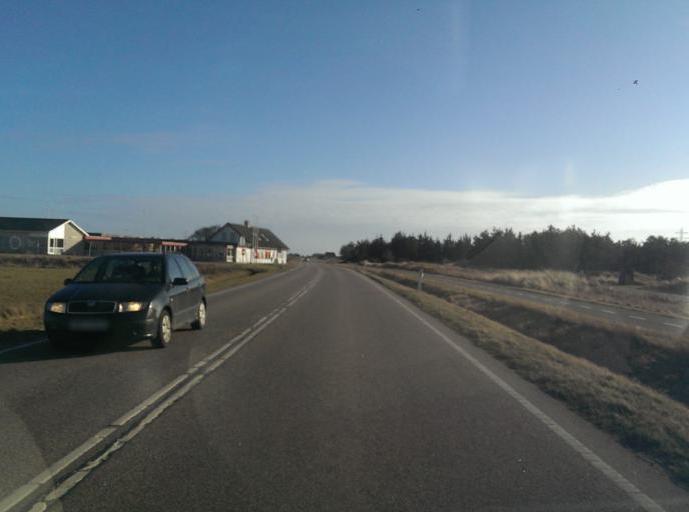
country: DK
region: Central Jutland
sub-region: Ringkobing-Skjern Kommune
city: Hvide Sande
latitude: 56.0815
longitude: 8.1198
